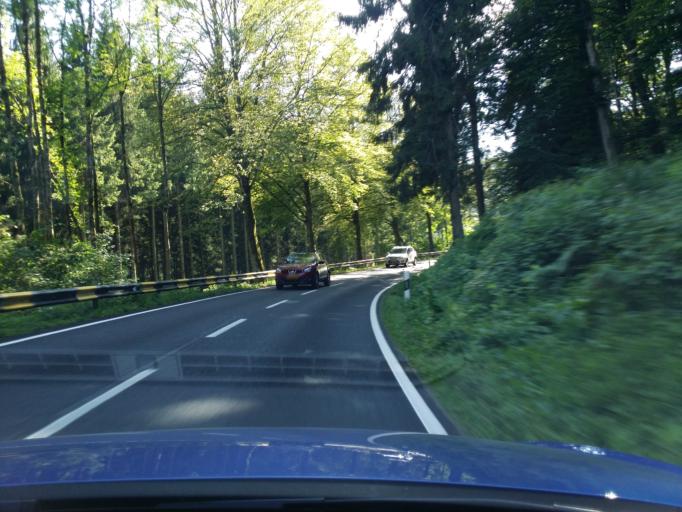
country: LU
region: Luxembourg
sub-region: Canton de Capellen
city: Kopstal
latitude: 49.6493
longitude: 6.0569
